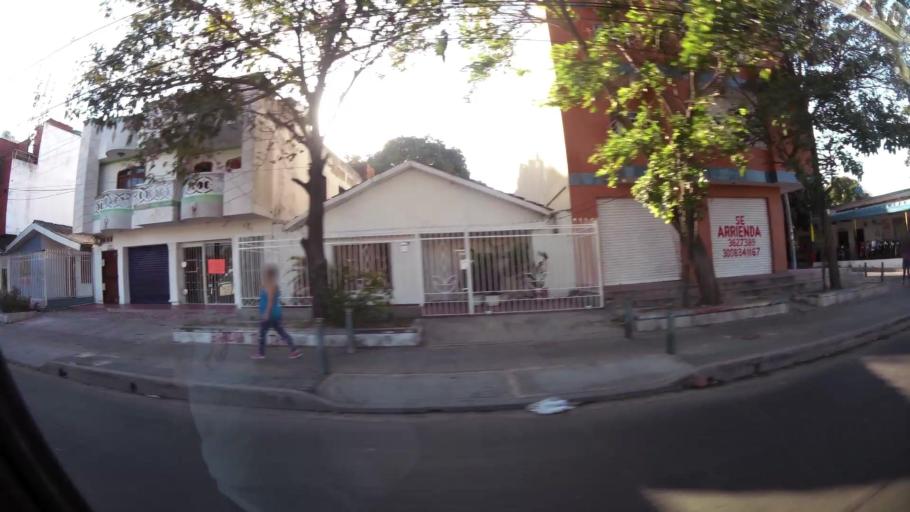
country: CO
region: Atlantico
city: Barranquilla
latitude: 10.9448
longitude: -74.7998
